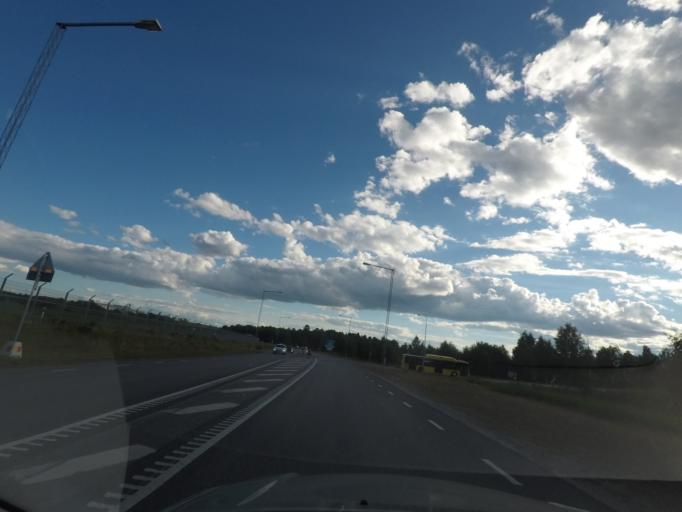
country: SE
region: Stockholm
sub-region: Sigtuna Kommun
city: Rosersberg
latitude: 59.6475
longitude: 17.9435
